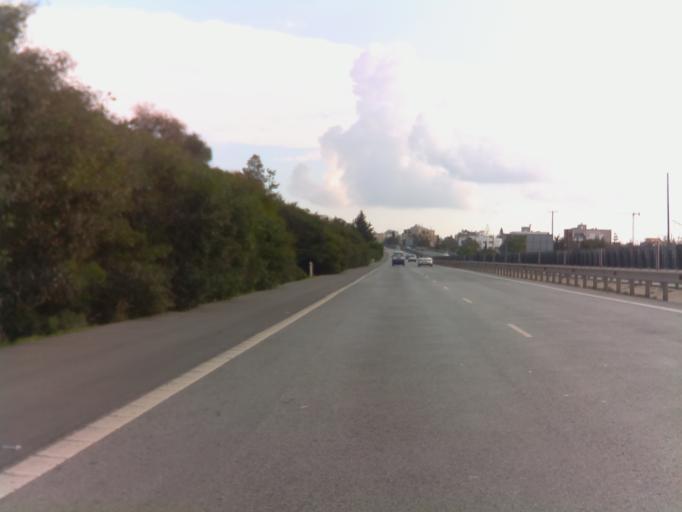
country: CY
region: Limassol
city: Mouttagiaka
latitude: 34.7091
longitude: 33.1154
